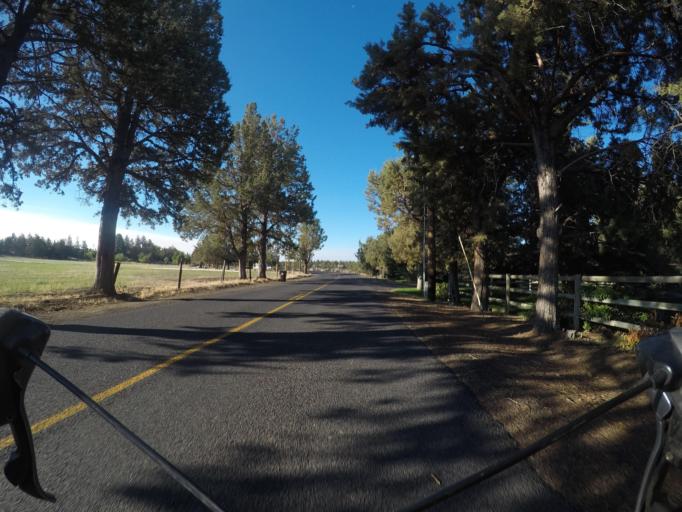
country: US
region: Oregon
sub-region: Deschutes County
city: Redmond
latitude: 44.2688
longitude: -121.2509
